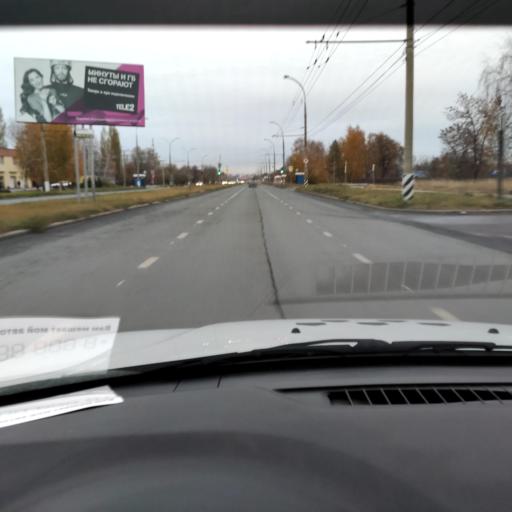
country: RU
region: Samara
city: Tol'yatti
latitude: 53.5420
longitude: 49.3007
